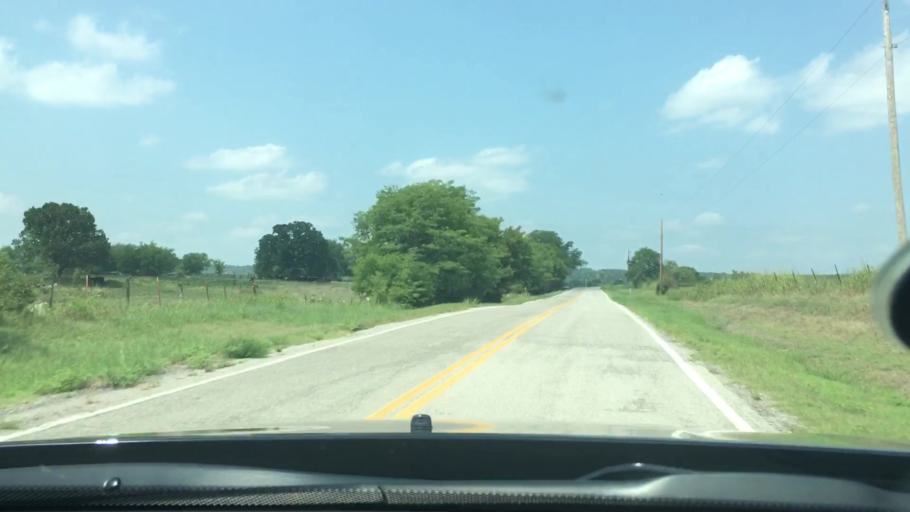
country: US
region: Oklahoma
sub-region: Johnston County
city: Tishomingo
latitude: 34.4027
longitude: -96.4962
